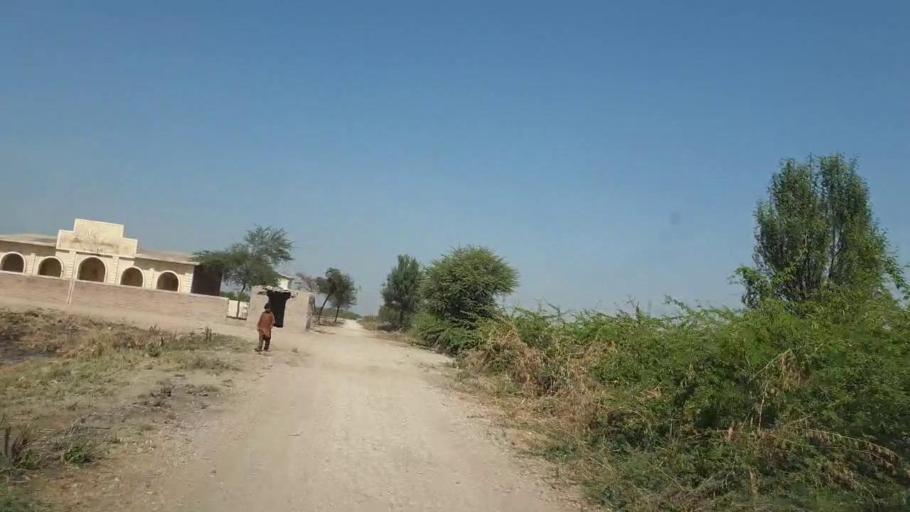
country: PK
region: Sindh
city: Kunri
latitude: 25.0975
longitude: 69.4583
